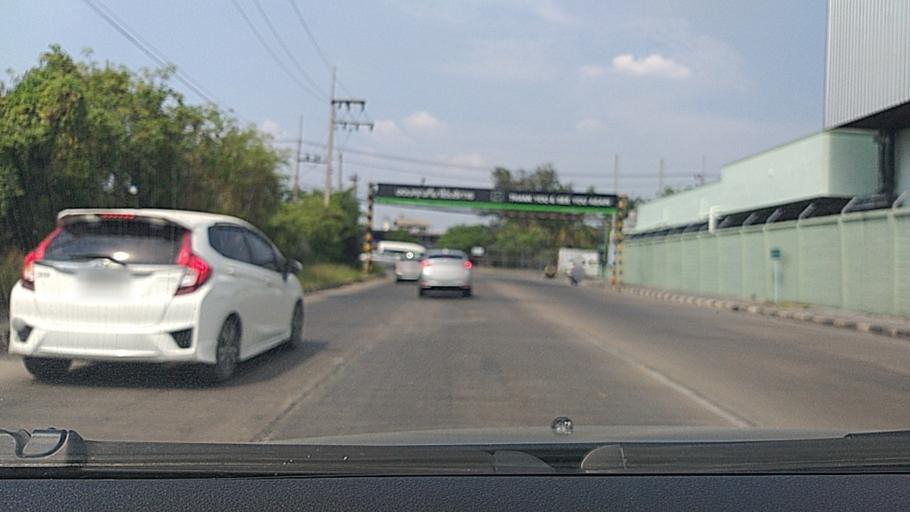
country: TH
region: Phra Nakhon Si Ayutthaya
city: Ban Bang Kadi Pathum Thani
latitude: 13.9977
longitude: 100.6180
